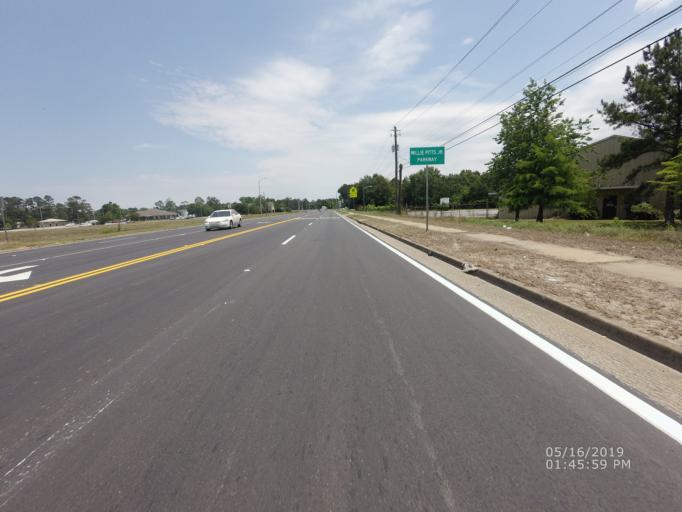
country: US
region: Georgia
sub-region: Dougherty County
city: Albany
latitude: 31.5490
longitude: -84.1744
